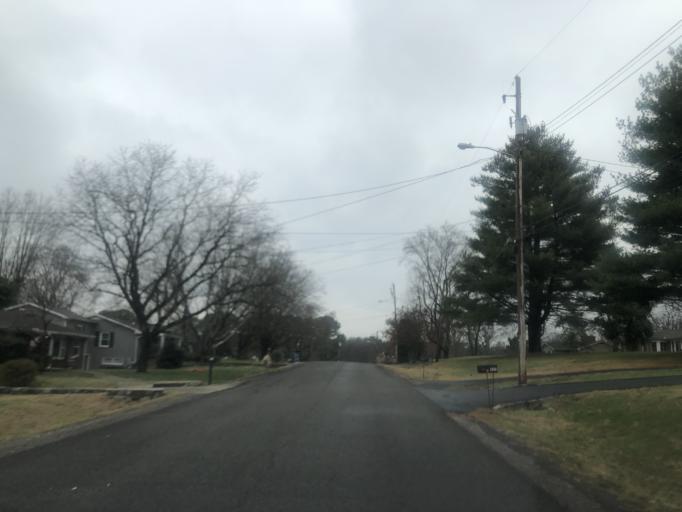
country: US
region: Tennessee
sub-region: Davidson County
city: Lakewood
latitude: 36.1720
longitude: -86.6873
